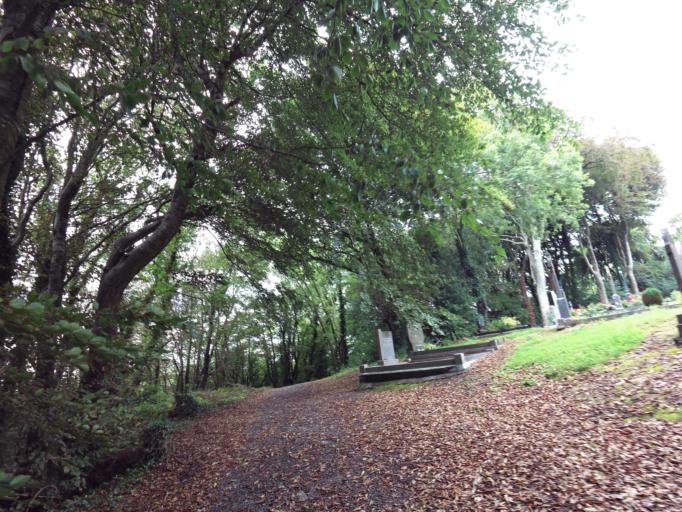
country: IE
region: Connaught
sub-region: County Galway
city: Gaillimh
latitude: 53.3002
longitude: -9.0778
